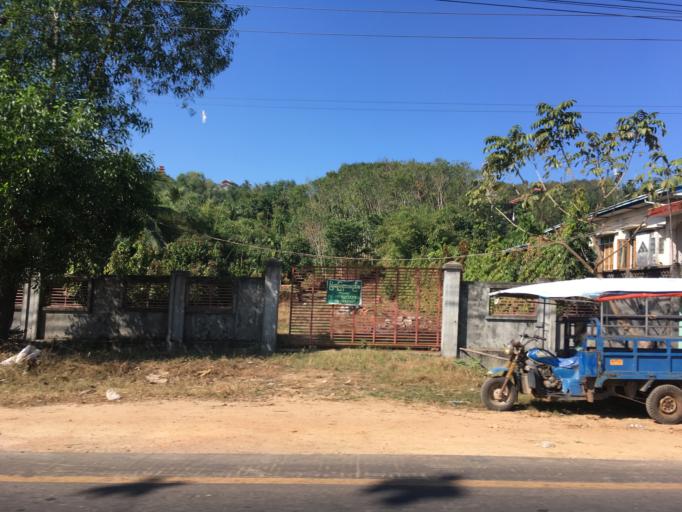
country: MM
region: Mon
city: Mawlamyine
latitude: 16.4761
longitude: 97.6332
